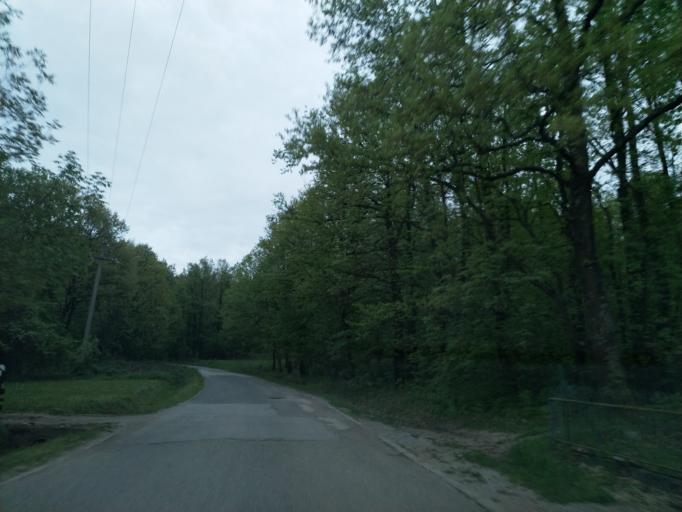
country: RS
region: Central Serbia
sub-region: Pomoravski Okrug
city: Cuprija
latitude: 43.9506
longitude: 21.4869
